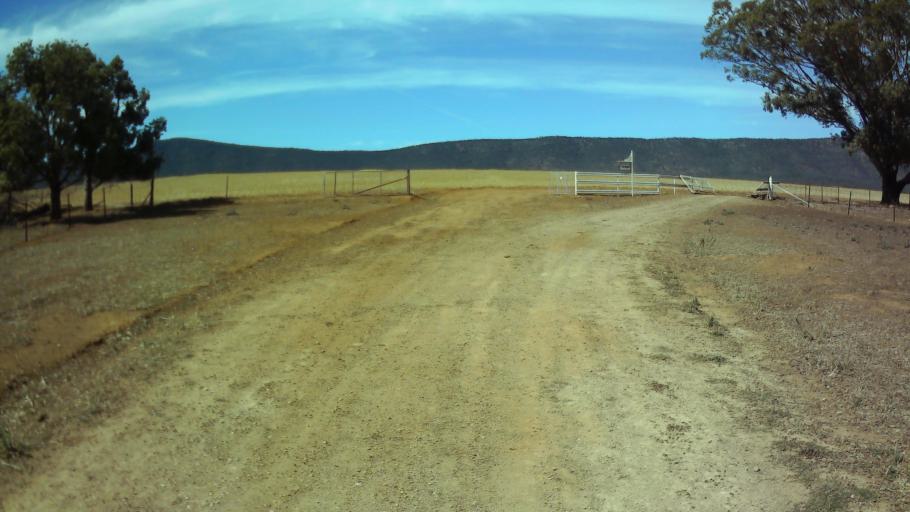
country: AU
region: New South Wales
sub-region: Weddin
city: Grenfell
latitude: -33.9503
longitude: 148.0661
